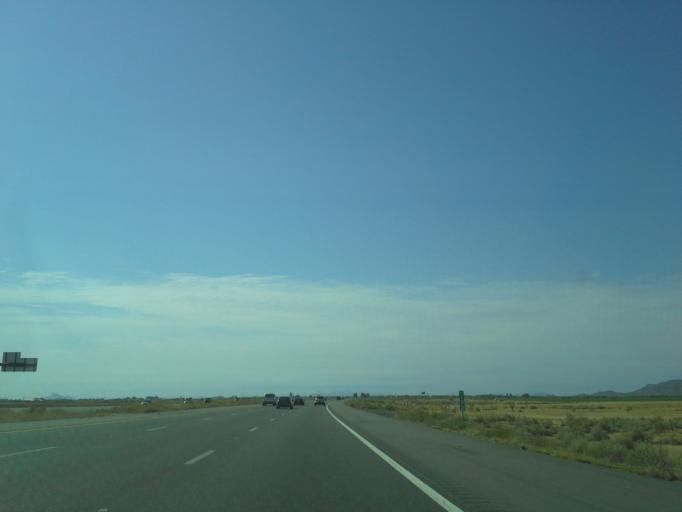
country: US
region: Arizona
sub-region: Pinal County
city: Casa Grande
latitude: 32.9220
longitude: -111.6893
